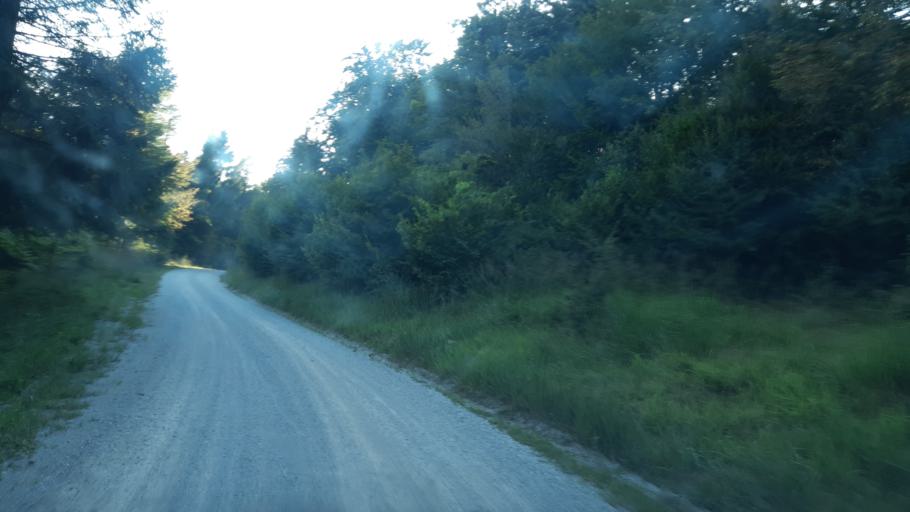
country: SI
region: Kocevje
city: Kocevje
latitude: 45.6669
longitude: 14.9421
